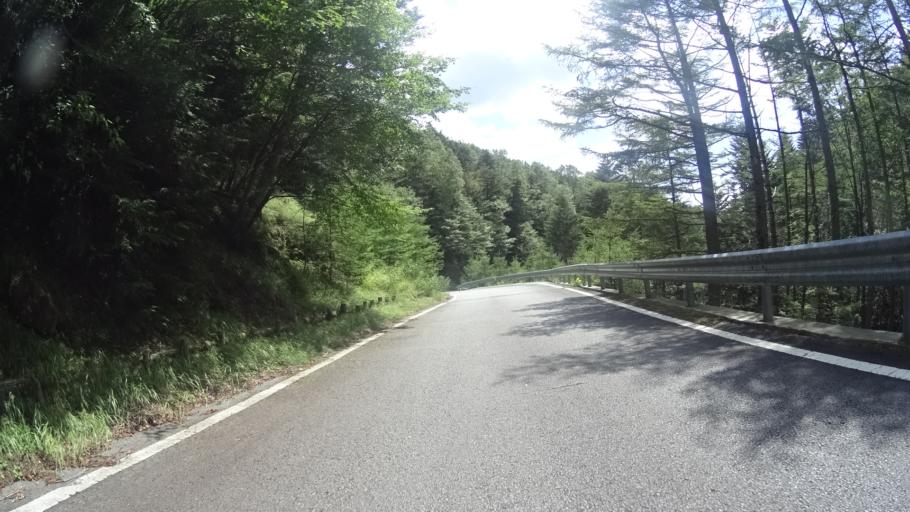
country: JP
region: Yamanashi
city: Enzan
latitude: 35.8532
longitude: 138.6448
